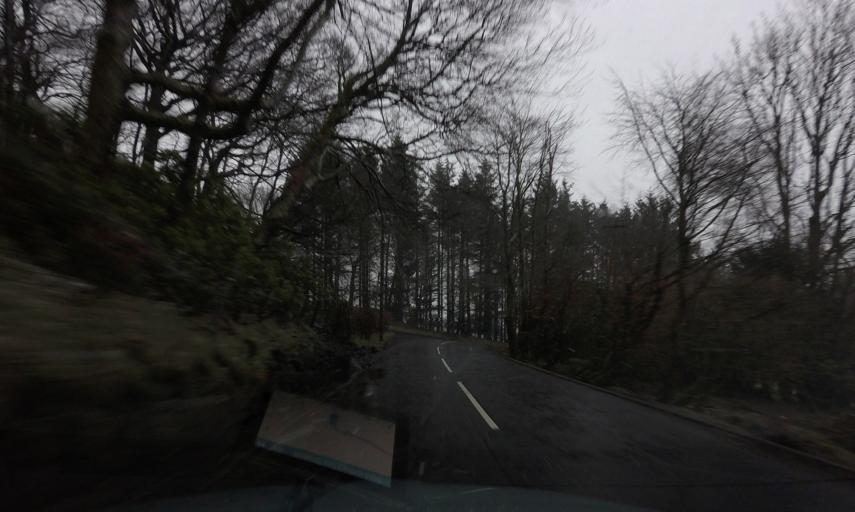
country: GB
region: Scotland
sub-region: North Lanarkshire
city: Shotts
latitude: 55.8333
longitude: -3.8268
